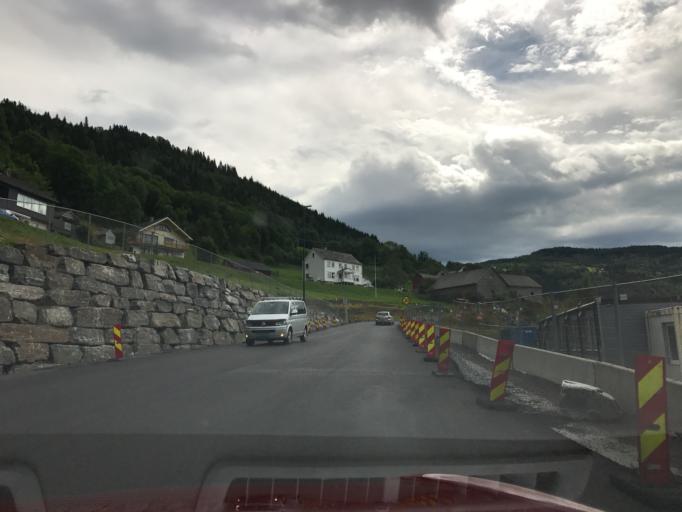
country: NO
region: Hordaland
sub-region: Granvin
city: Granvin
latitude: 60.5665
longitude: 6.7236
